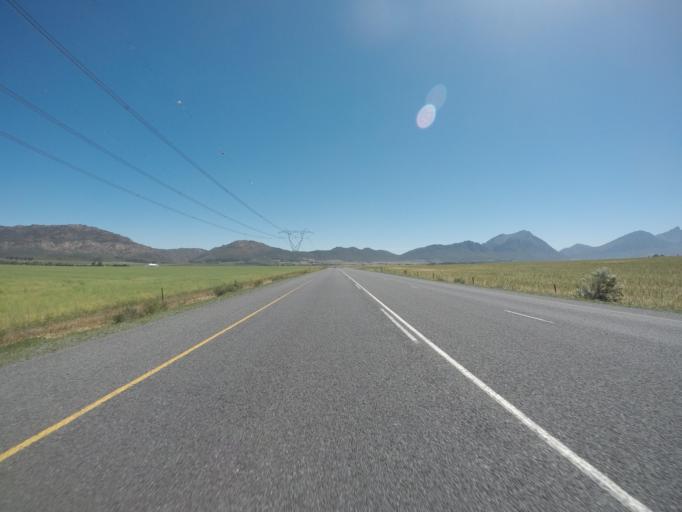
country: ZA
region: Western Cape
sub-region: Cape Winelands District Municipality
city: Ceres
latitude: -33.3188
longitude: 19.1357
